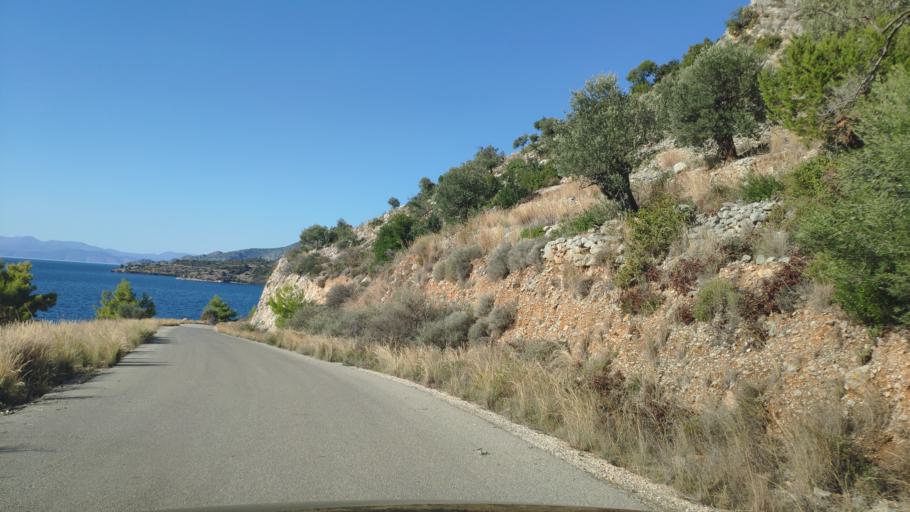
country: GR
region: Attica
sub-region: Nomos Piraios
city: Galatas
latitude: 37.5704
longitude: 23.3616
